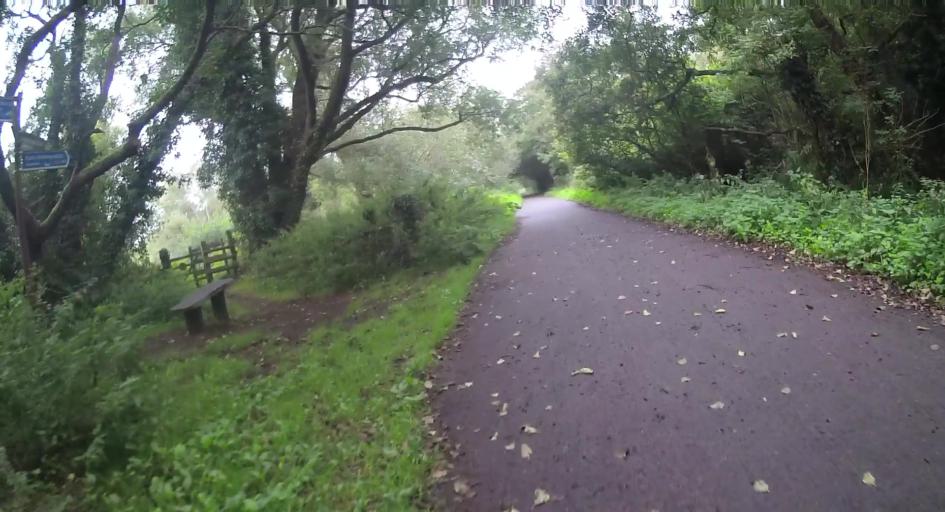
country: GB
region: England
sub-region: Isle of Wight
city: Newchurch
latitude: 50.6691
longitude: -1.1892
